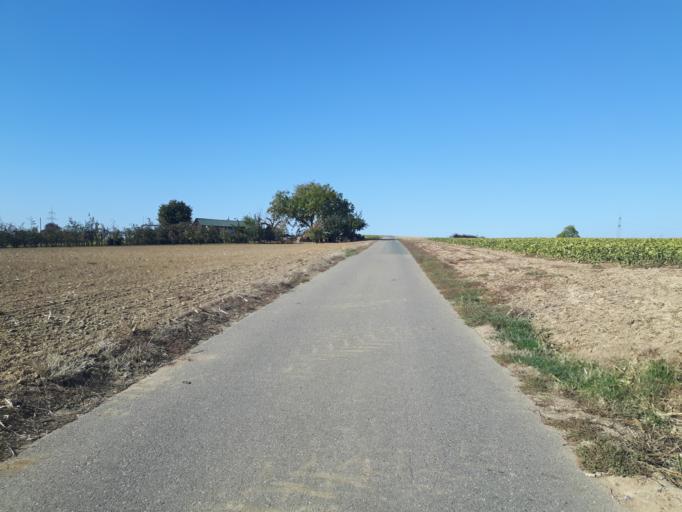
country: DE
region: Baden-Wuerttemberg
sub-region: Regierungsbezirk Stuttgart
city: Leingarten
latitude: 49.1587
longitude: 9.1654
